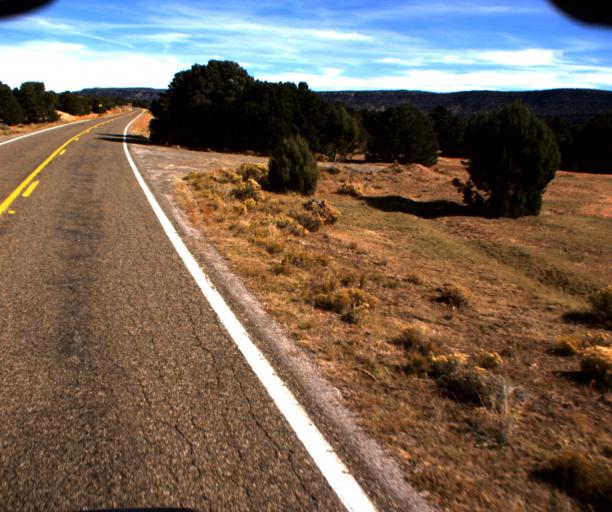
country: US
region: Arizona
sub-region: Navajo County
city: Kayenta
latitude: 36.5696
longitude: -110.4996
